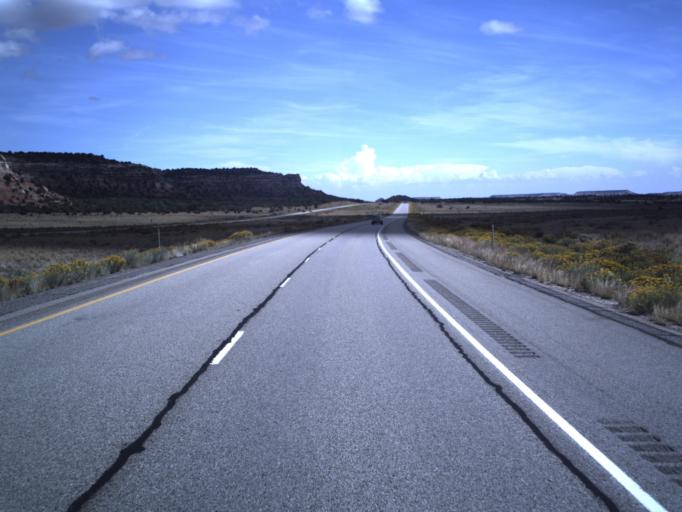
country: US
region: Utah
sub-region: Emery County
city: Castle Dale
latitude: 38.8746
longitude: -110.7422
